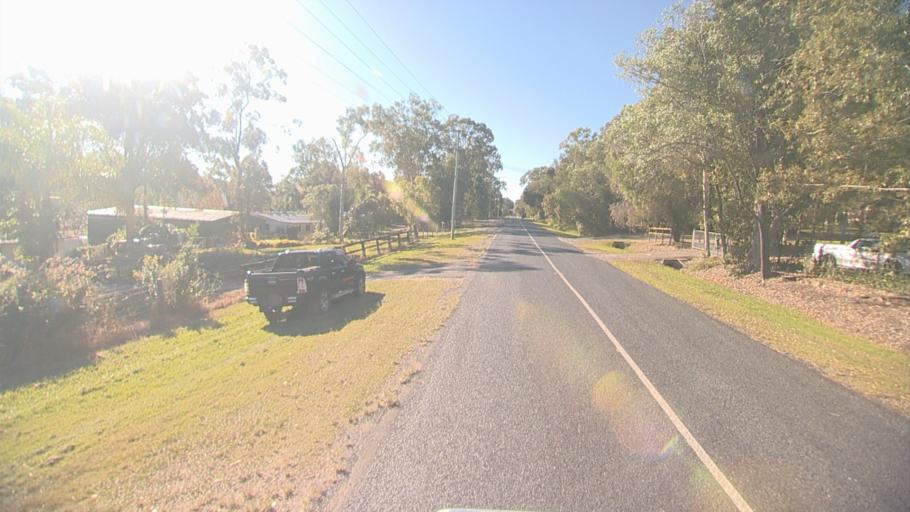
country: AU
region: Queensland
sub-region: Logan
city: Logan Reserve
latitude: -27.7392
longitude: 153.1029
